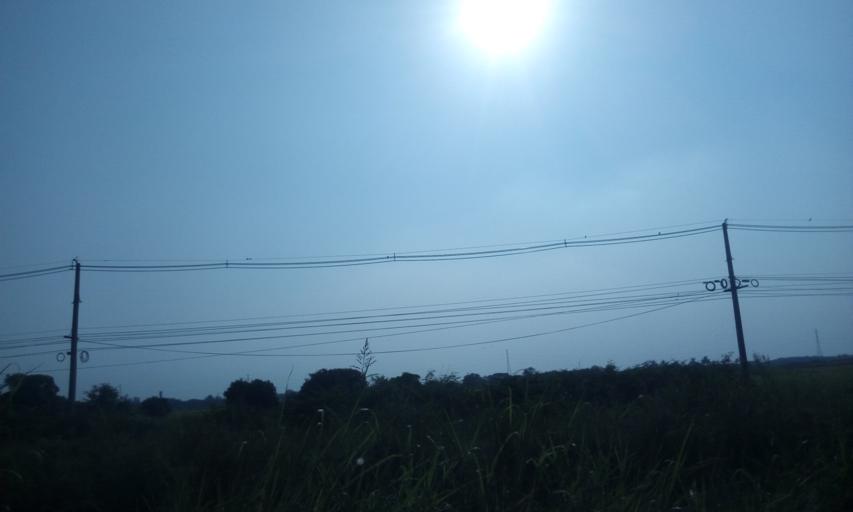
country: TH
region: Sing Buri
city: Phrom Buri
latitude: 14.8167
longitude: 100.4328
